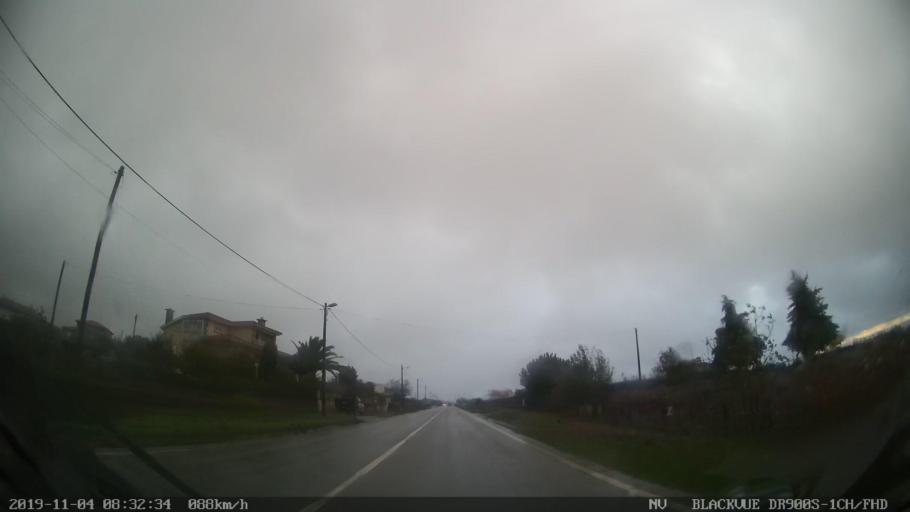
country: PT
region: Vila Real
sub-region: Sabrosa
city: Sabrosa
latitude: 41.2626
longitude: -7.6003
